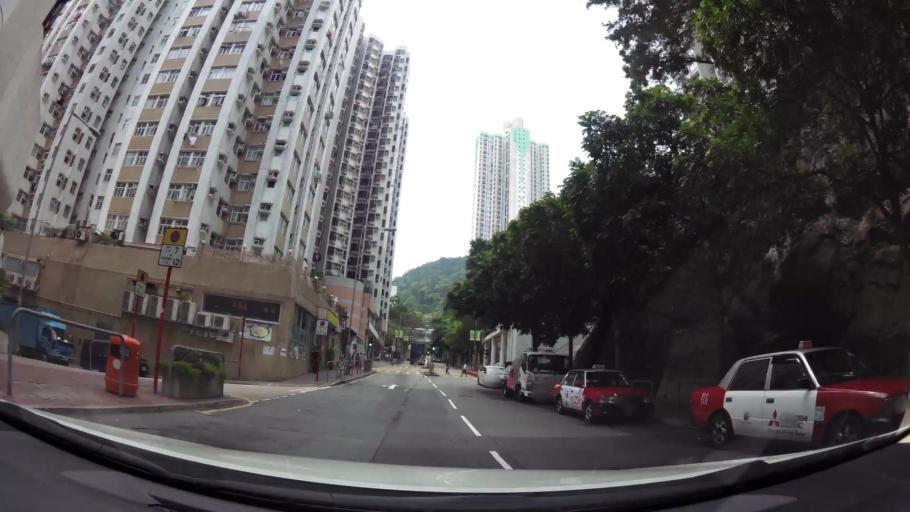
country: HK
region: Wanchai
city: Wan Chai
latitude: 22.2784
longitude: 114.2255
